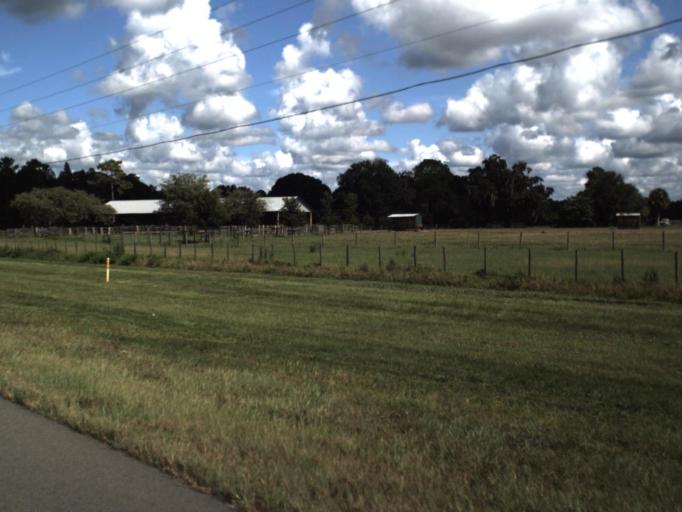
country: US
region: Florida
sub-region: Pasco County
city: Zephyrhills North
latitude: 28.2511
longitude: -82.0610
